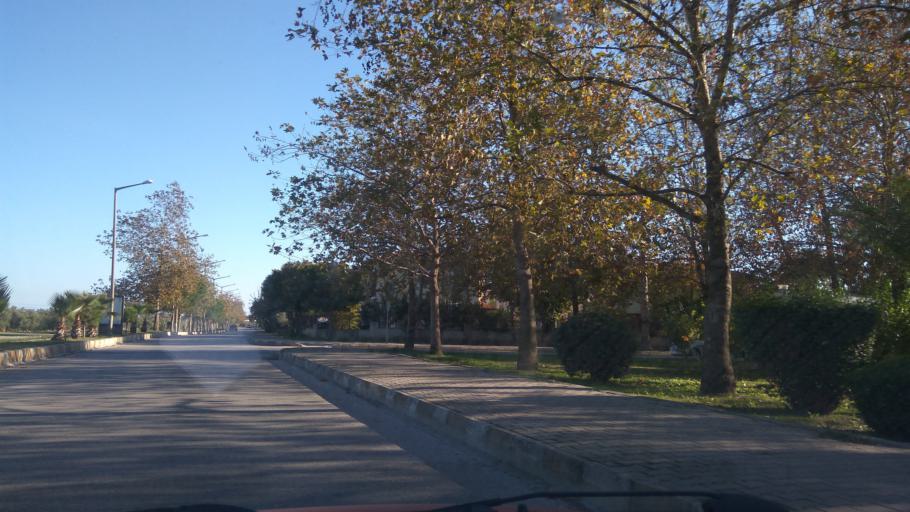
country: TR
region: Antalya
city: Kemer
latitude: 36.5711
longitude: 30.5572
